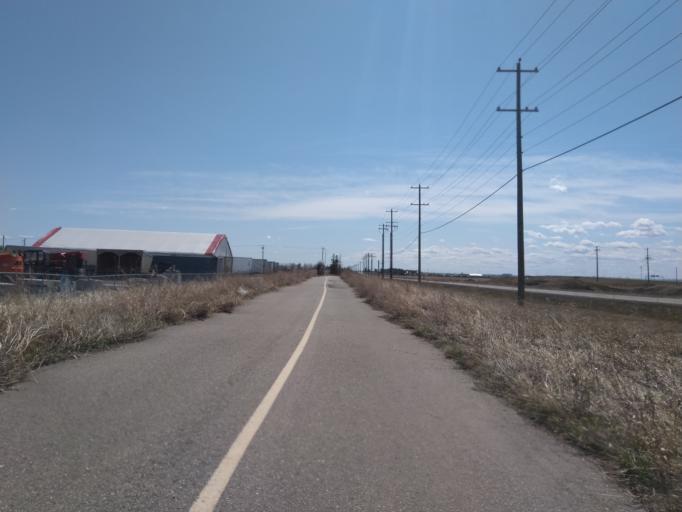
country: CA
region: Alberta
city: Chestermere
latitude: 50.9648
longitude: -113.9115
